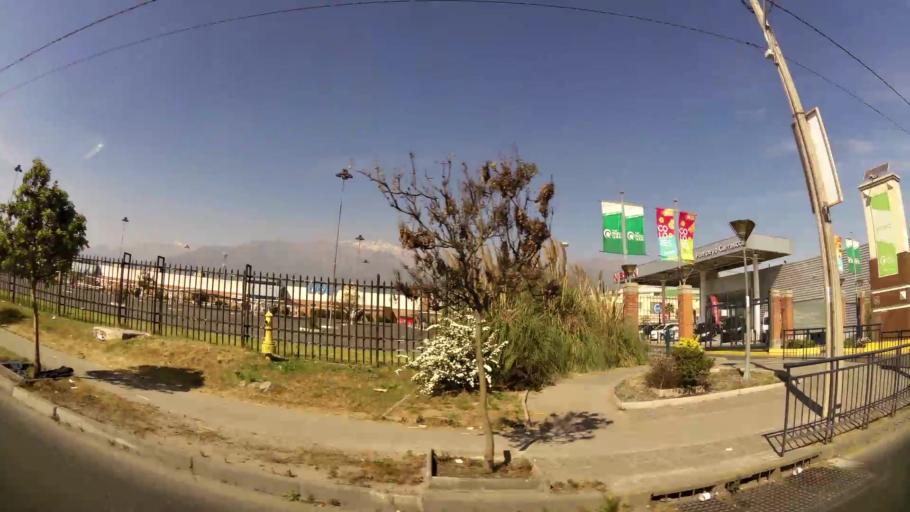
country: CL
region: Santiago Metropolitan
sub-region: Provincia de Santiago
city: Villa Presidente Frei, Nunoa, Santiago, Chile
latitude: -33.4864
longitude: -70.5798
